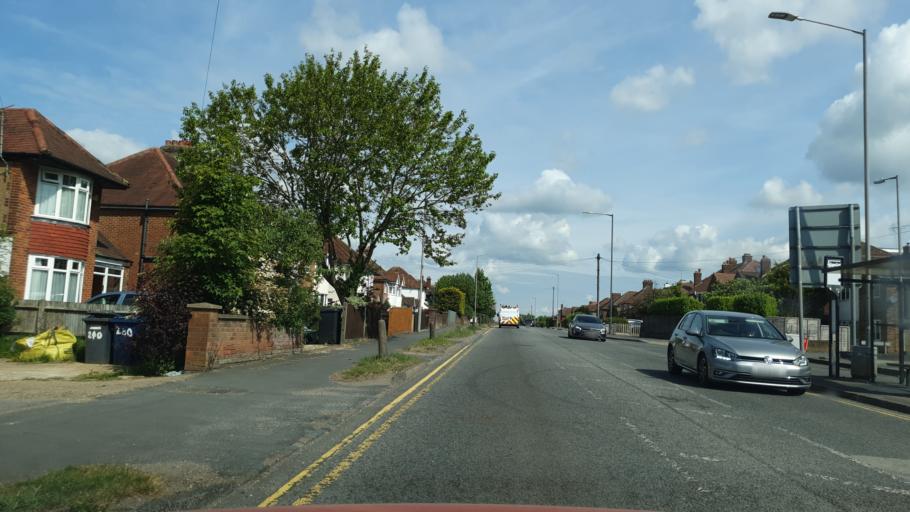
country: GB
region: England
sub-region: Buckinghamshire
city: High Wycombe
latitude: 51.6171
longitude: -0.7832
